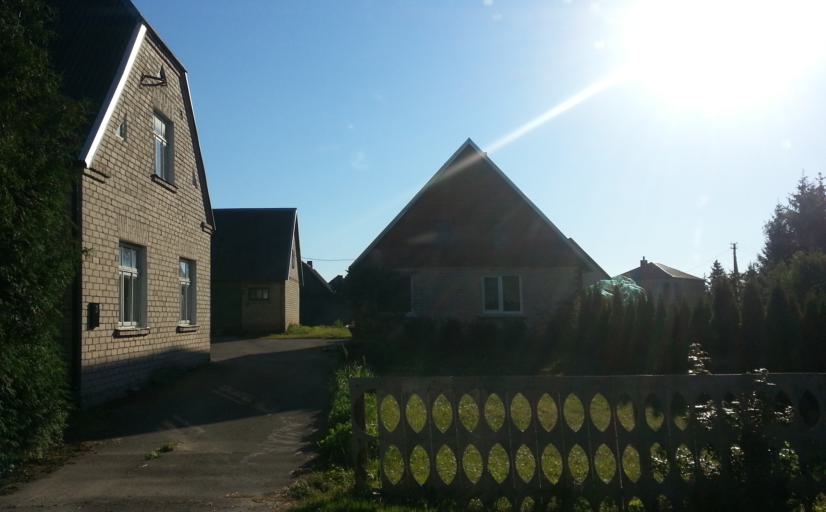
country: LT
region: Panevezys
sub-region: Birzai
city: Birzai
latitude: 56.2044
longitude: 24.7258
